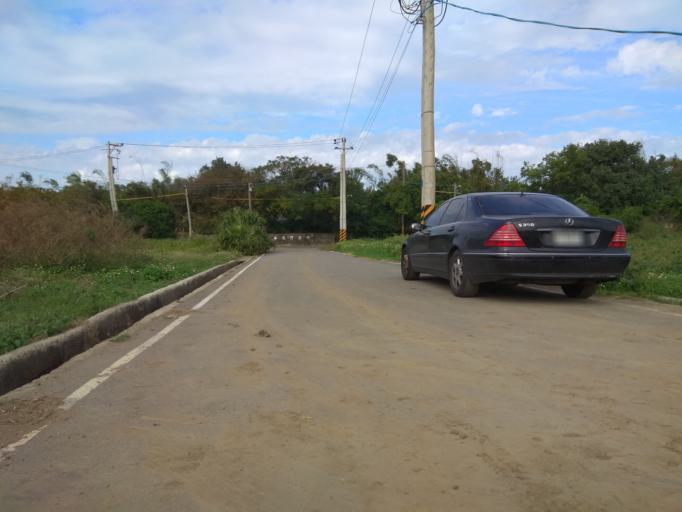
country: TW
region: Taiwan
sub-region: Hsinchu
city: Zhubei
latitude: 24.9612
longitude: 121.0062
